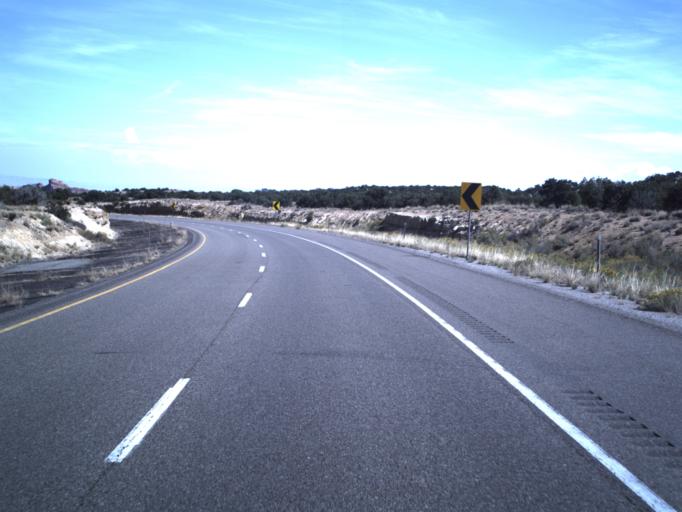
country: US
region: Utah
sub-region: Emery County
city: Castle Dale
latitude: 38.9132
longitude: -110.5091
